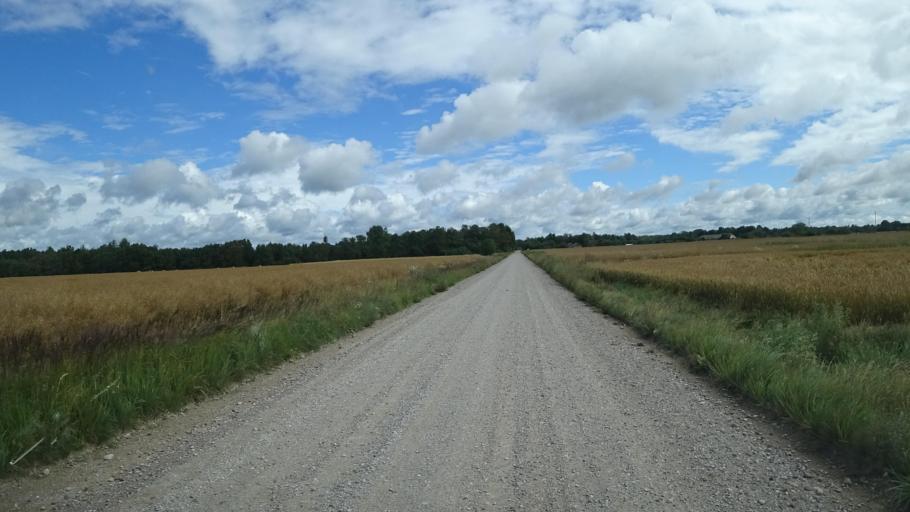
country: LV
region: Liepaja
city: Vec-Liepaja
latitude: 56.6583
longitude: 21.0641
